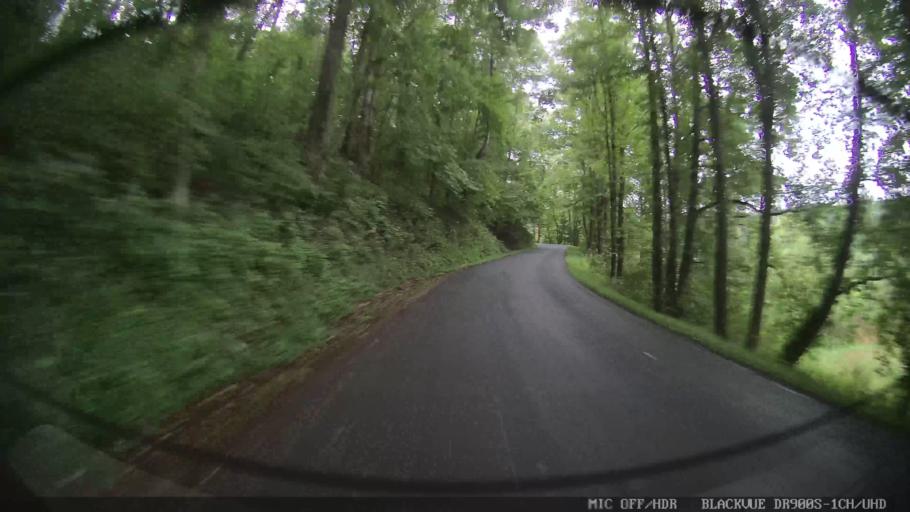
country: US
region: Georgia
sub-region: Gilmer County
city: Ellijay
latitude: 34.7664
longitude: -84.5326
